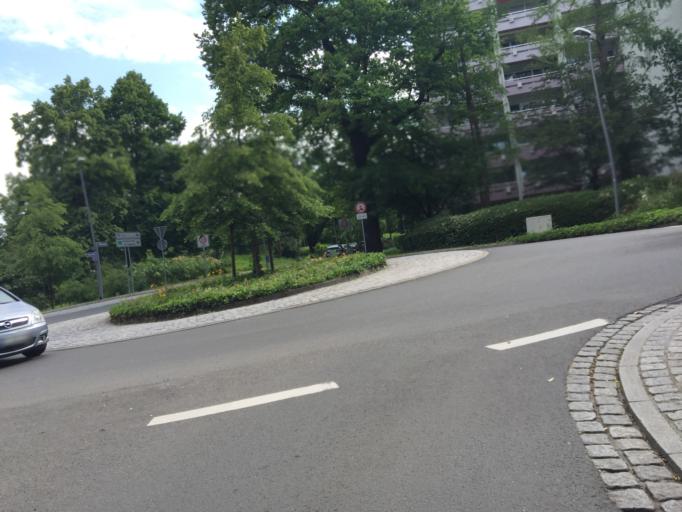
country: DE
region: Hesse
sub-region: Regierungsbezirk Darmstadt
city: Wiesbaden
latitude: 50.0869
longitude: 8.2598
